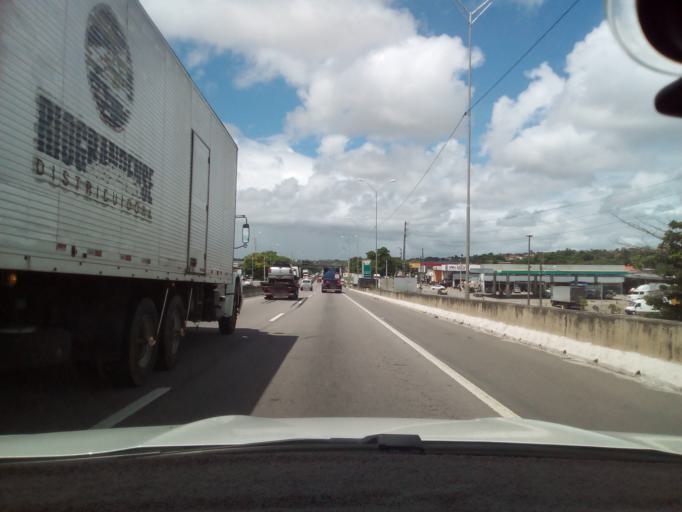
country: BR
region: Paraiba
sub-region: Bayeux
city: Bayeux
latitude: -7.1326
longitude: -34.9310
